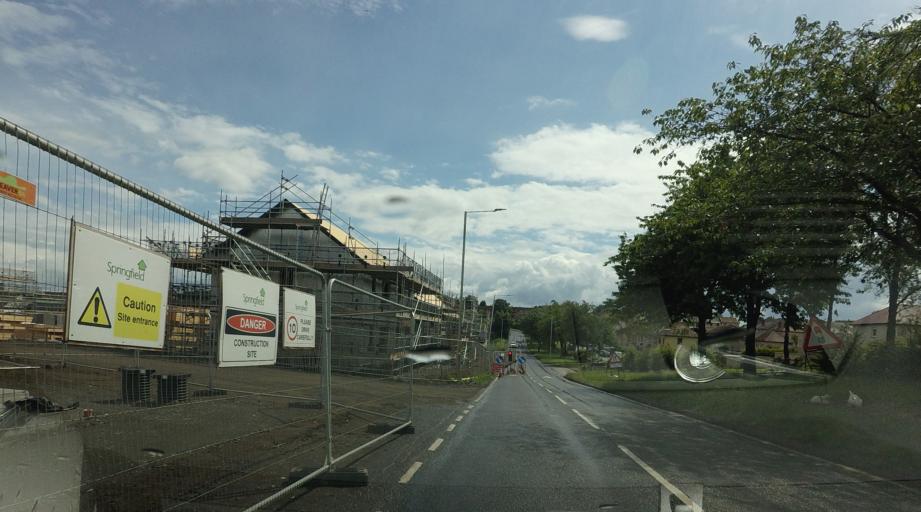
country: GB
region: Scotland
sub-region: Fife
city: Ballingry
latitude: 56.1647
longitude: -3.3217
